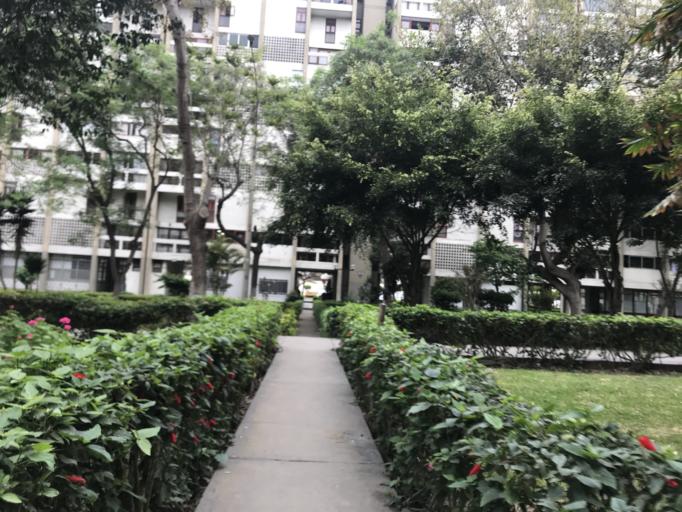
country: PE
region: Lima
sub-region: Lima
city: San Isidro
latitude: -12.0886
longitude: -77.0541
